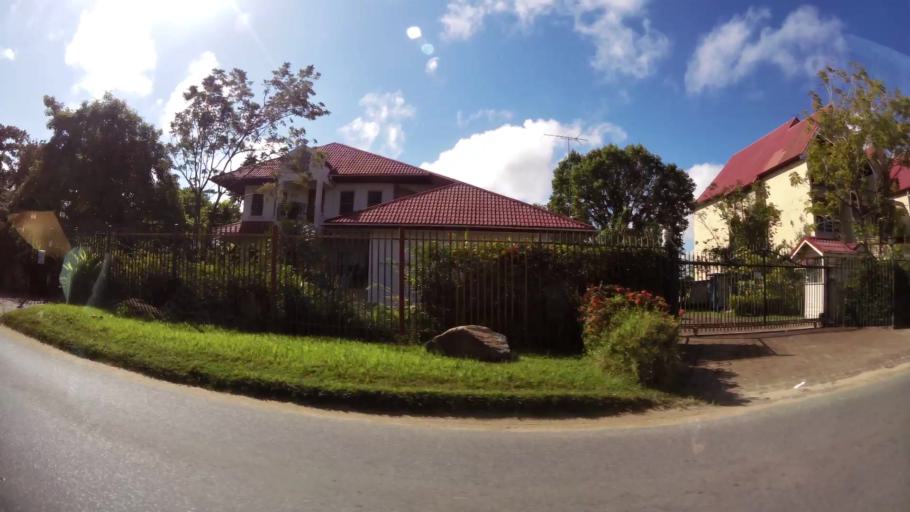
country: SR
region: Commewijne
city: Nieuw Amsterdam
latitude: 5.8504
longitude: -55.1084
